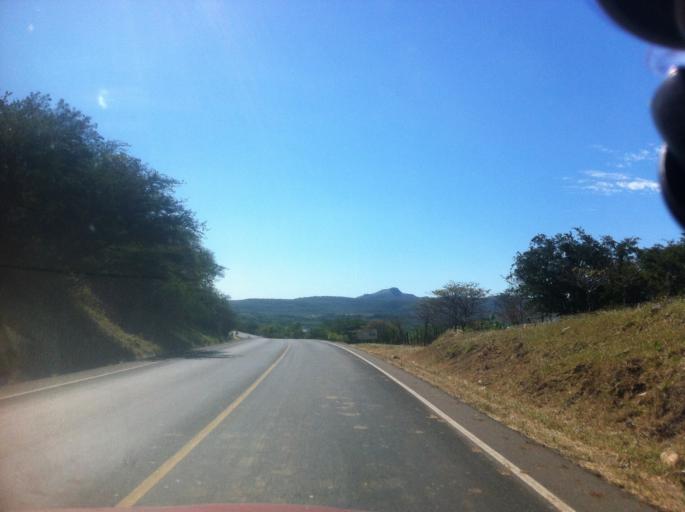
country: NI
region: Boaco
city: Teustepe
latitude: 12.3555
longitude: -85.9207
